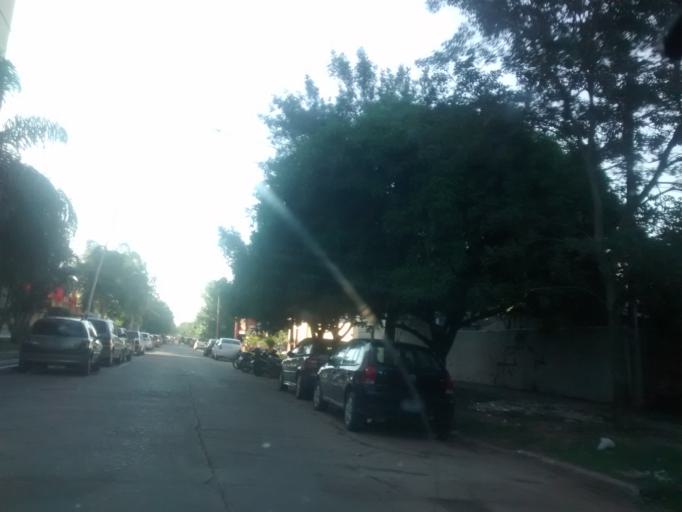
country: AR
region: Chaco
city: Resistencia
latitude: -27.4413
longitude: -59.0012
